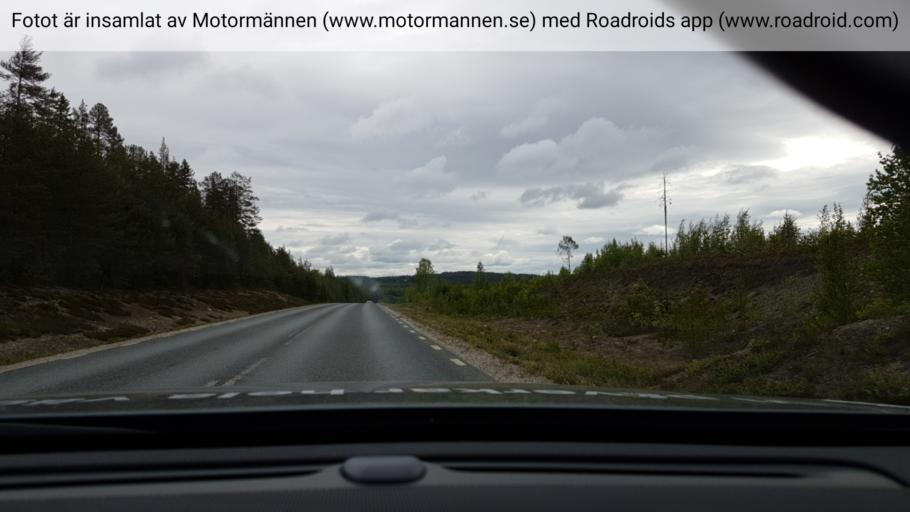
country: SE
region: Vaesterbotten
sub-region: Lycksele Kommun
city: Lycksele
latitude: 64.5102
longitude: 18.3325
